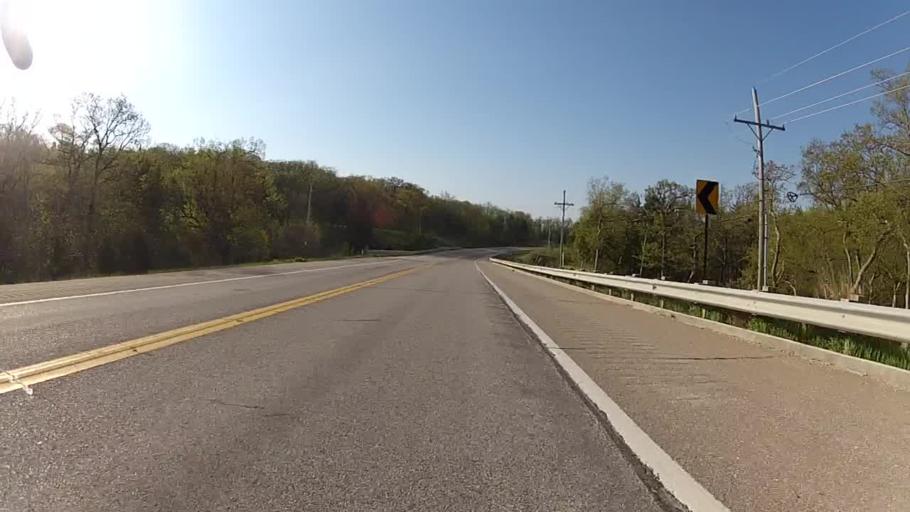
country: US
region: Kansas
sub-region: Riley County
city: Manhattan
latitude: 39.1679
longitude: -96.6433
